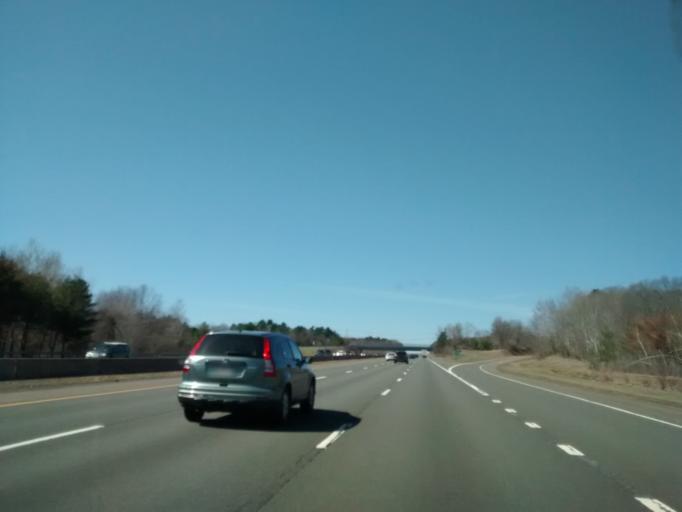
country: US
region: Connecticut
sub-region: Tolland County
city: Tolland
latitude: 41.8881
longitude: -72.3083
